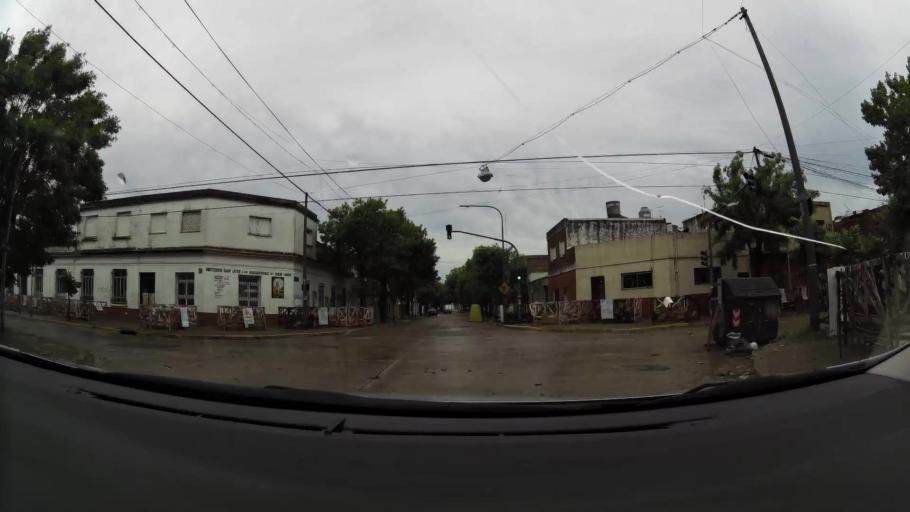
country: AR
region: Buenos Aires F.D.
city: Villa Lugano
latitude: -34.6634
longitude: -58.4415
